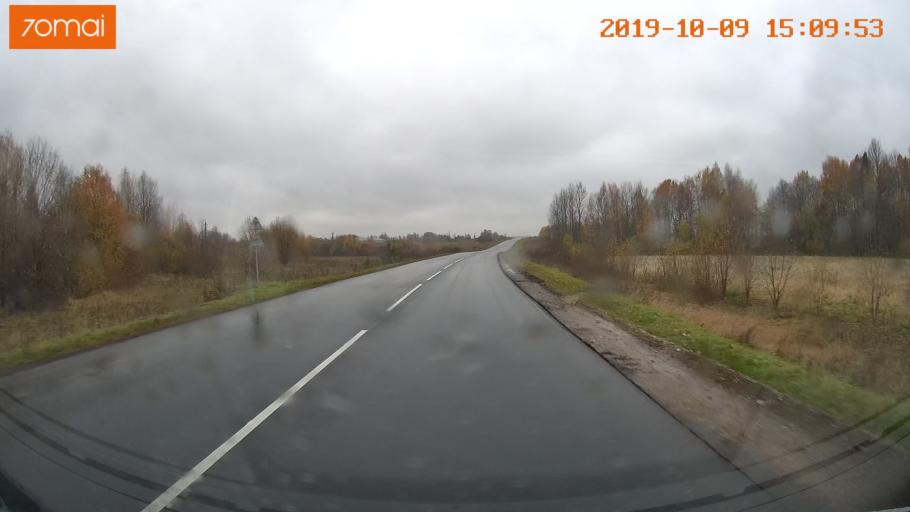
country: RU
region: Kostroma
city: Susanino
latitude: 58.1853
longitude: 41.6478
